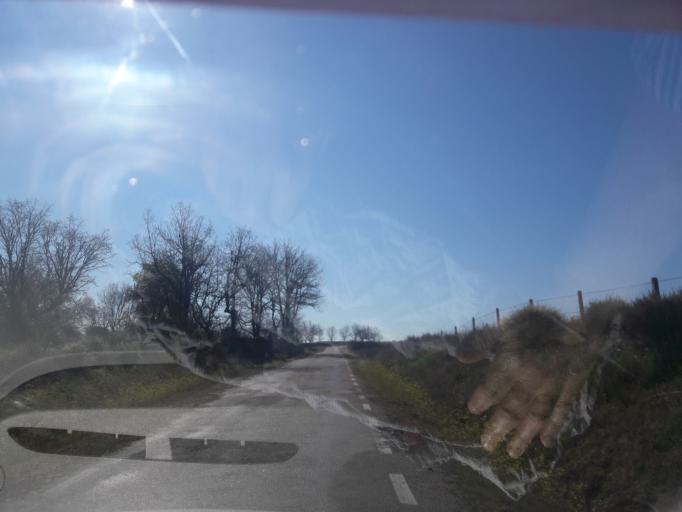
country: ES
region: Castille and Leon
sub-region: Provincia de Salamanca
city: Valsalabroso
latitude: 41.1701
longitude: -6.5038
